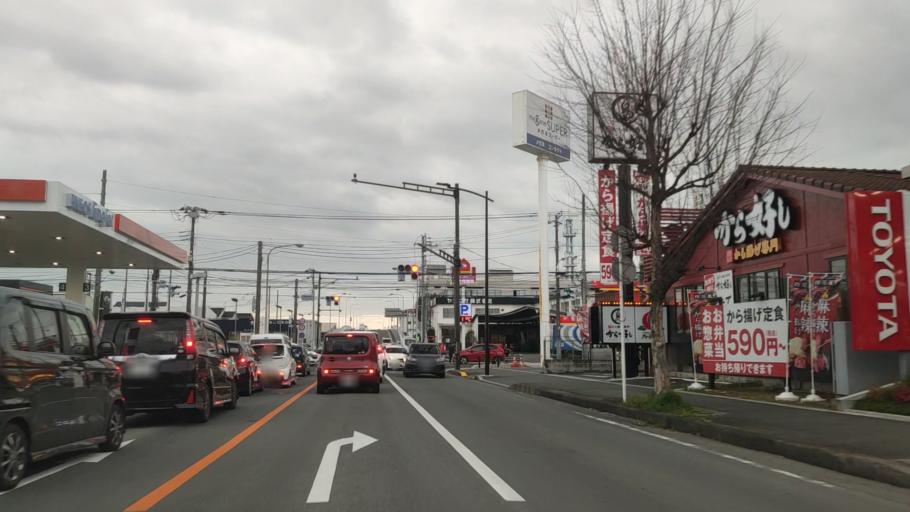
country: JP
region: Kanagawa
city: Odawara
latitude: 35.2805
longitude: 139.1893
